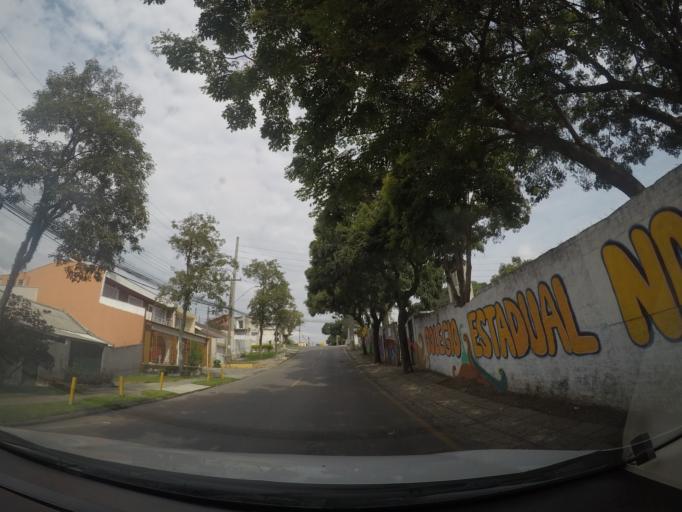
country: BR
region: Parana
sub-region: Sao Jose Dos Pinhais
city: Sao Jose dos Pinhais
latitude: -25.5169
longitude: -49.2759
